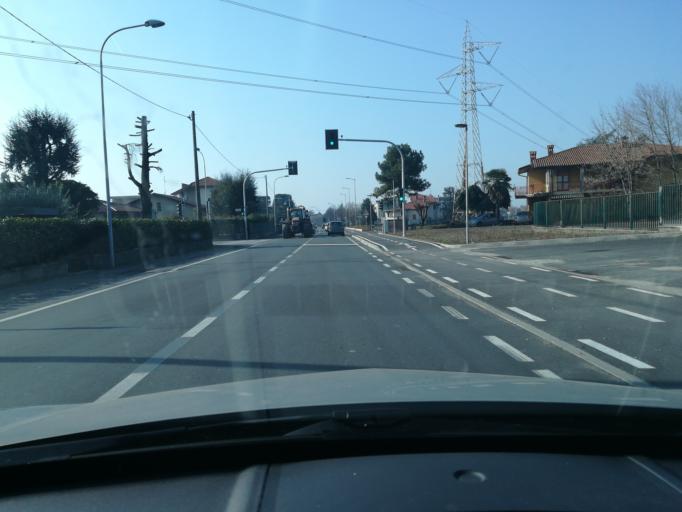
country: IT
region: Lombardy
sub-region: Provincia di Bergamo
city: Zanica
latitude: 45.6443
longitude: 9.6945
